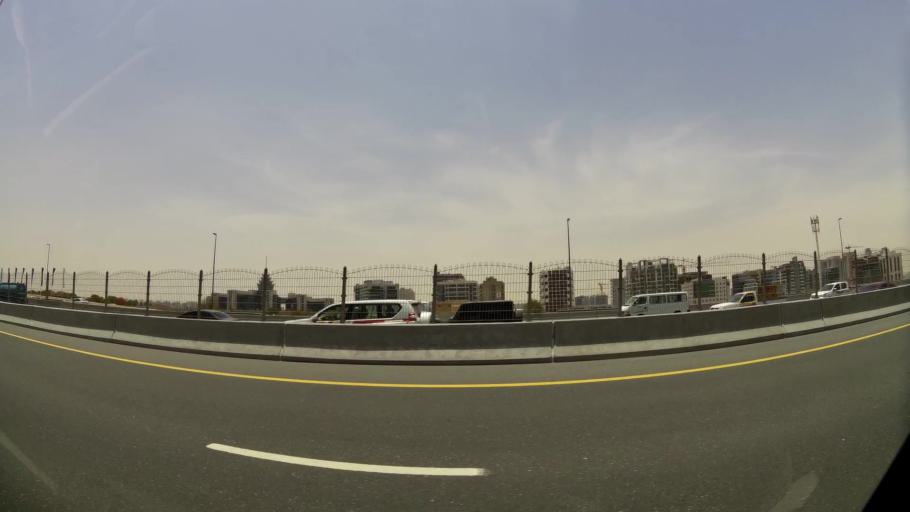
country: AE
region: Dubai
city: Dubai
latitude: 25.1263
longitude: 55.3729
